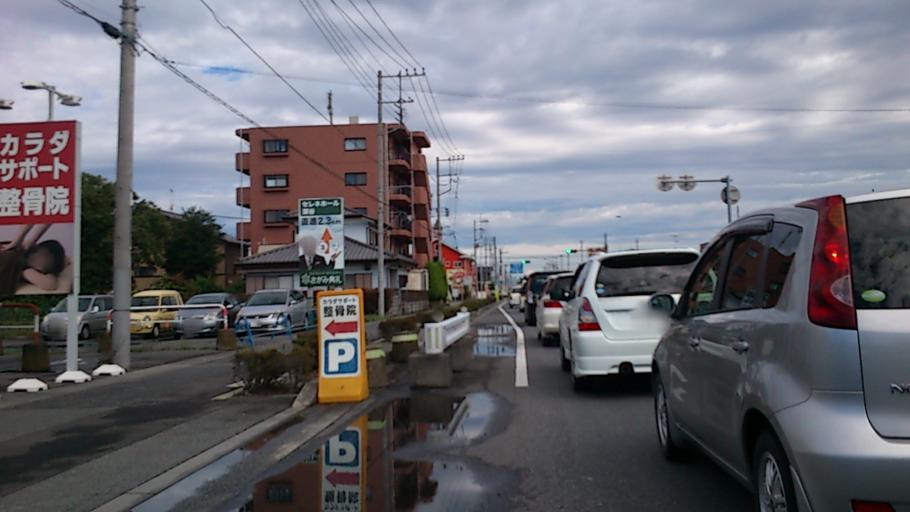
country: JP
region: Saitama
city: Fukayacho
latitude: 36.1762
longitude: 139.3352
